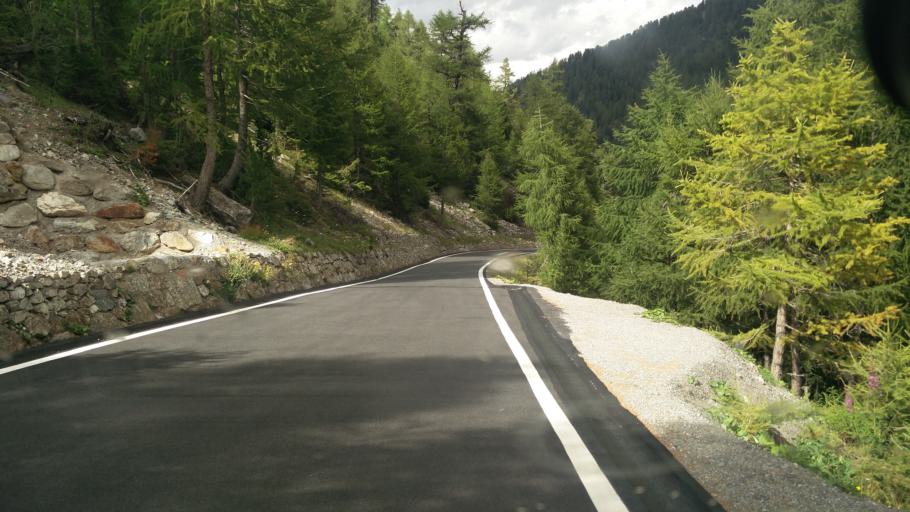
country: IT
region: Trentino-Alto Adige
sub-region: Bolzano
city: Tubre
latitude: 46.5729
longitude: 10.4373
